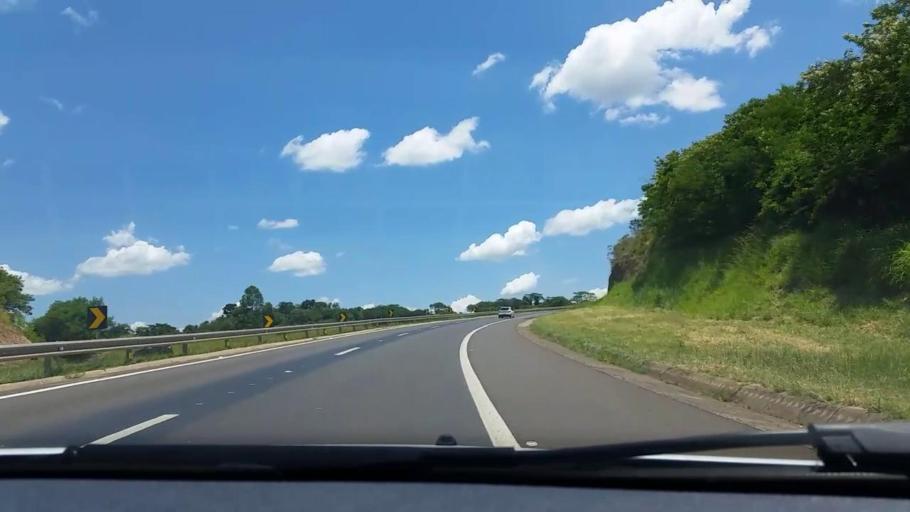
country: BR
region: Sao Paulo
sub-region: Bauru
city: Bauru
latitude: -22.4342
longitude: -49.1338
